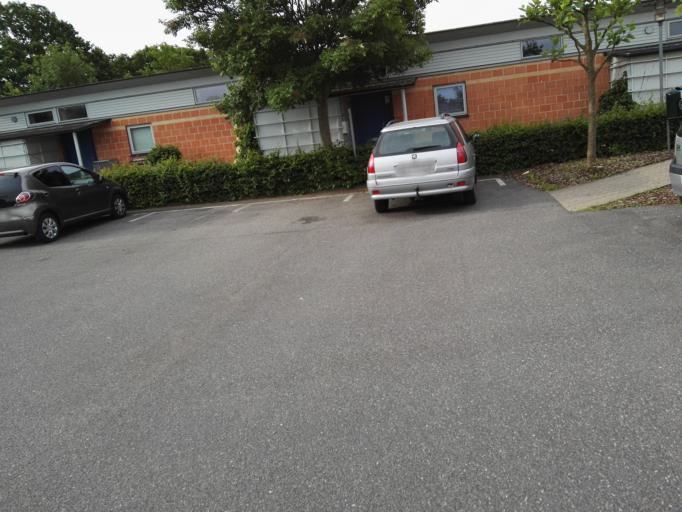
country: DK
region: Capital Region
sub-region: Ballerup Kommune
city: Ballerup
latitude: 55.7401
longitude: 12.3640
